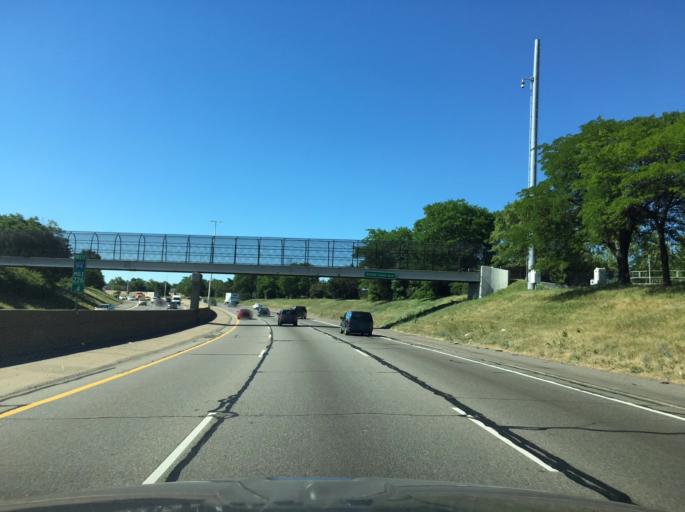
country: US
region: Michigan
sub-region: Wayne County
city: Grosse Pointe Woods
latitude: 42.4591
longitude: -82.9243
